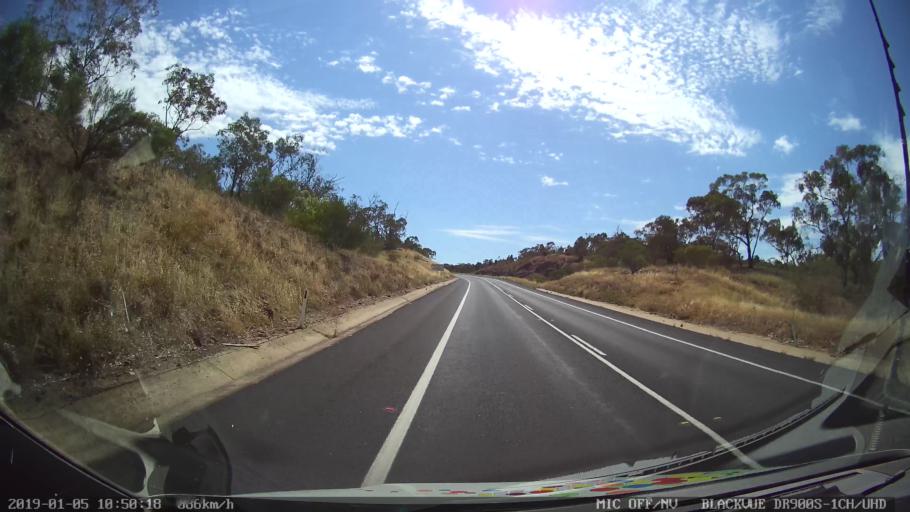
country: AU
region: New South Wales
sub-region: Warrumbungle Shire
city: Coonabarabran
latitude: -31.4295
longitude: 149.0734
